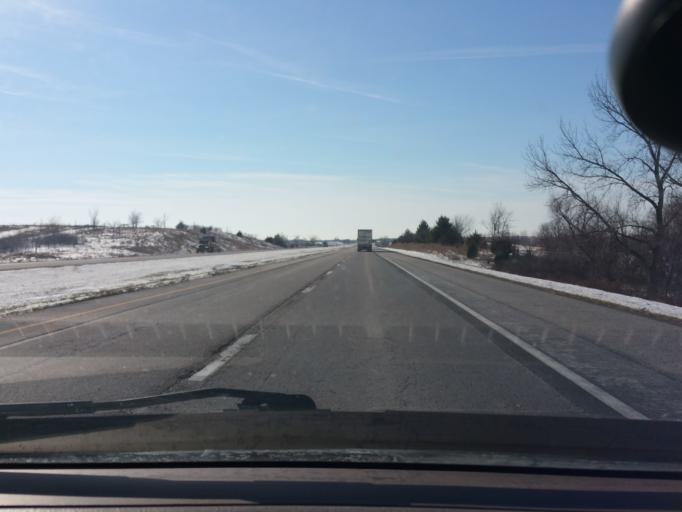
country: US
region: Missouri
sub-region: Harrison County
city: Bethany
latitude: 40.1676
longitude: -94.0240
